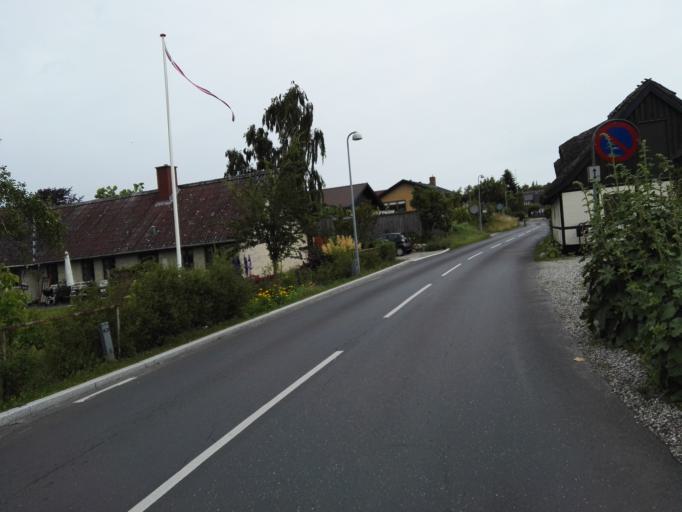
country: DK
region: Zealand
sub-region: Roskilde Kommune
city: Jyllinge
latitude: 55.7546
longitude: 12.1036
